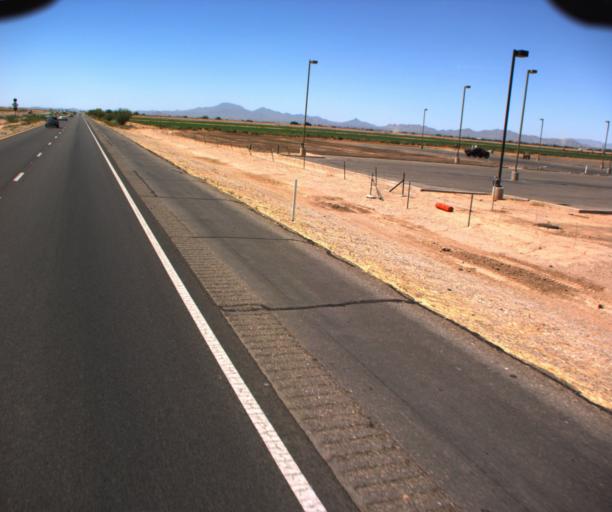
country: US
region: Arizona
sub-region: Pinal County
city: Maricopa
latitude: 33.0233
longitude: -112.0480
